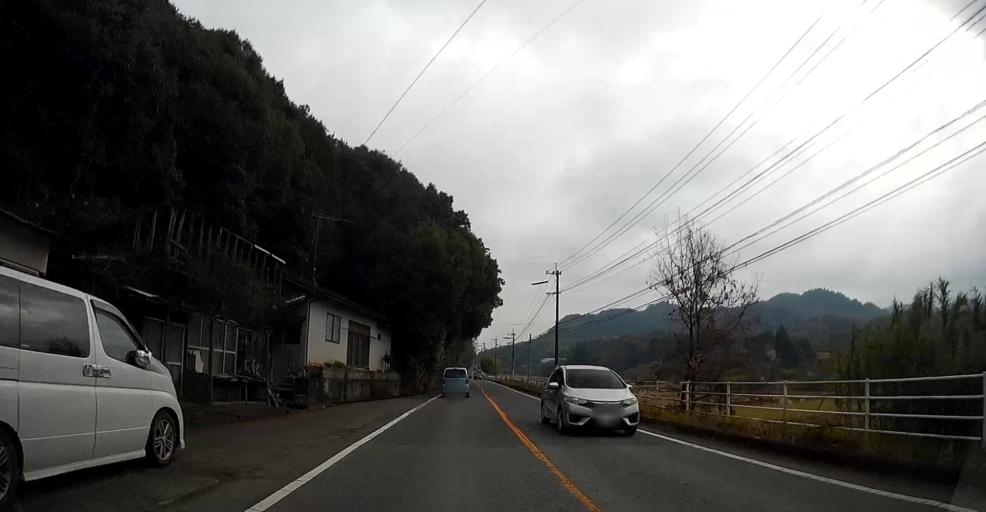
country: JP
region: Kumamoto
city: Matsubase
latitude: 32.6478
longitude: 130.7222
